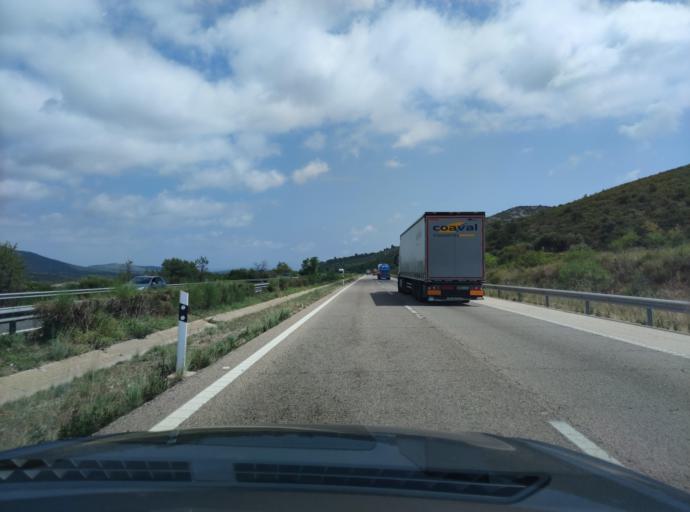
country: ES
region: Valencia
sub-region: Provincia de Castello
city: Santa Magdalena de Pulpis
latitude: 40.3751
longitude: 0.3359
